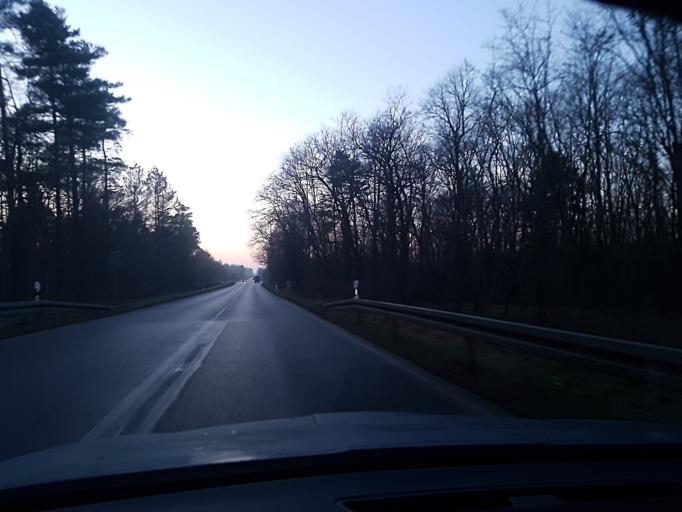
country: DE
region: Brandenburg
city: Schonewalde
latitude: 51.6350
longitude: 13.6345
